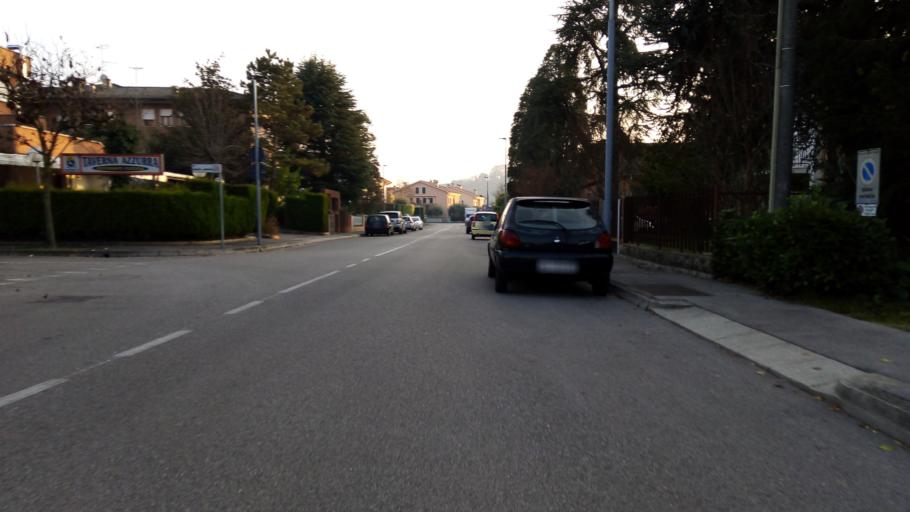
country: IT
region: Veneto
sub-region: Provincia di Padova
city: Abano Terme
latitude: 45.3530
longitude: 11.7647
